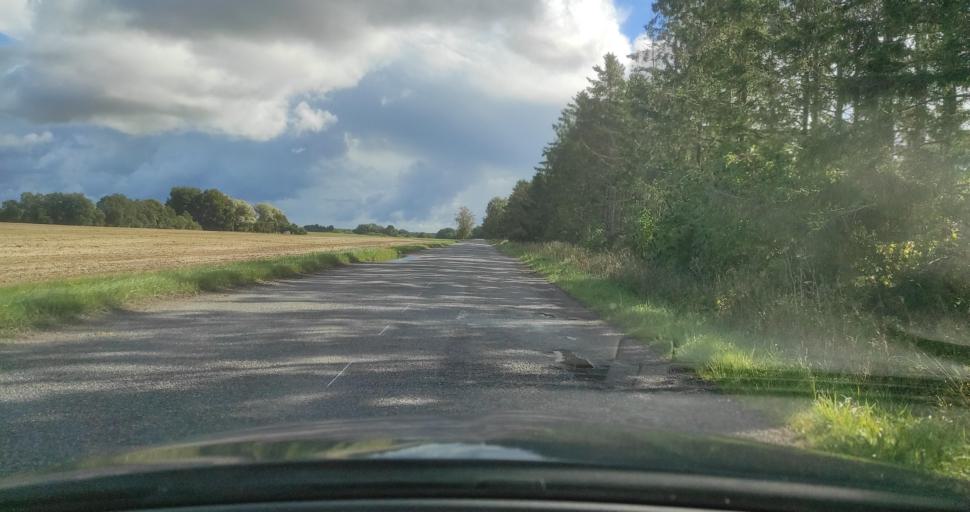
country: LV
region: Ventspils Rajons
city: Piltene
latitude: 57.2636
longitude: 21.5967
